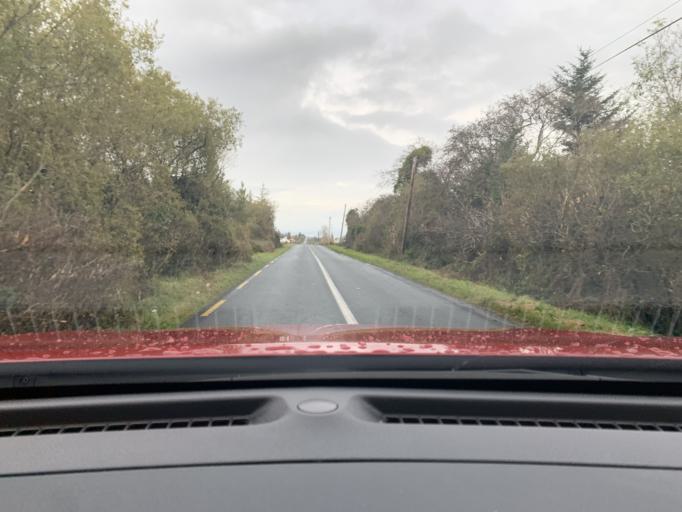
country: IE
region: Connaught
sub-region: Roscommon
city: Ballaghaderreen
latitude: 53.9627
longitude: -8.5410
